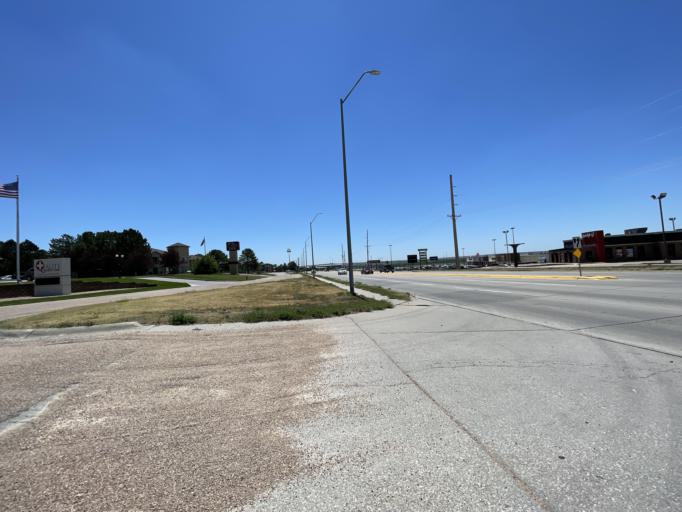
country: US
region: Nebraska
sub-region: Red Willow County
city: McCook
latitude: 40.2033
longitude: -100.6454
